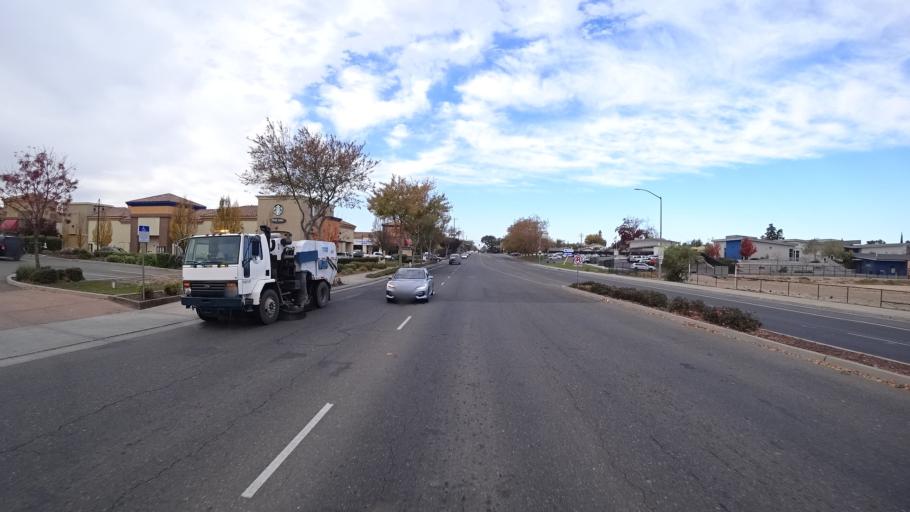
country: US
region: California
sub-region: Sacramento County
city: Citrus Heights
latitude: 38.6942
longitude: -121.2913
